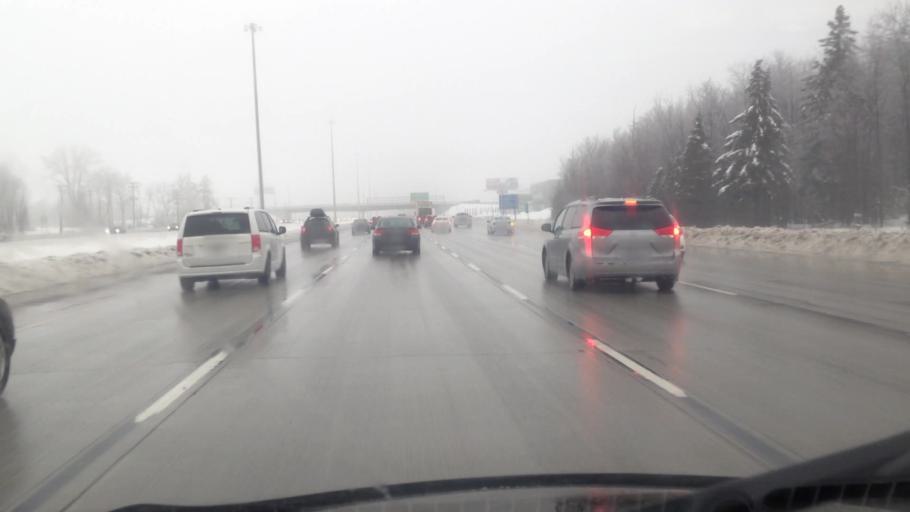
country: CA
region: Quebec
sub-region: Laurentides
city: Blainville
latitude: 45.6733
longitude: -73.9083
